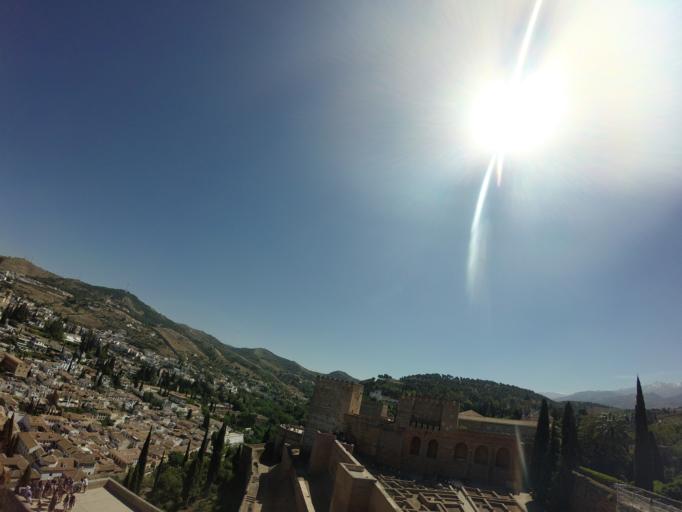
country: ES
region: Andalusia
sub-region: Provincia de Granada
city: Granada
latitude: 37.1770
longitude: -3.5923
